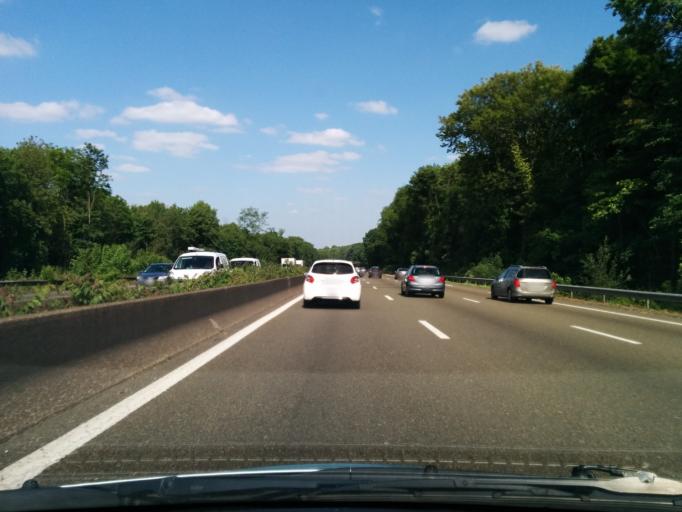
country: FR
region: Ile-de-France
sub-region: Departement des Hauts-de-Seine
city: Marnes-la-Coquette
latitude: 48.8348
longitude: 2.1734
